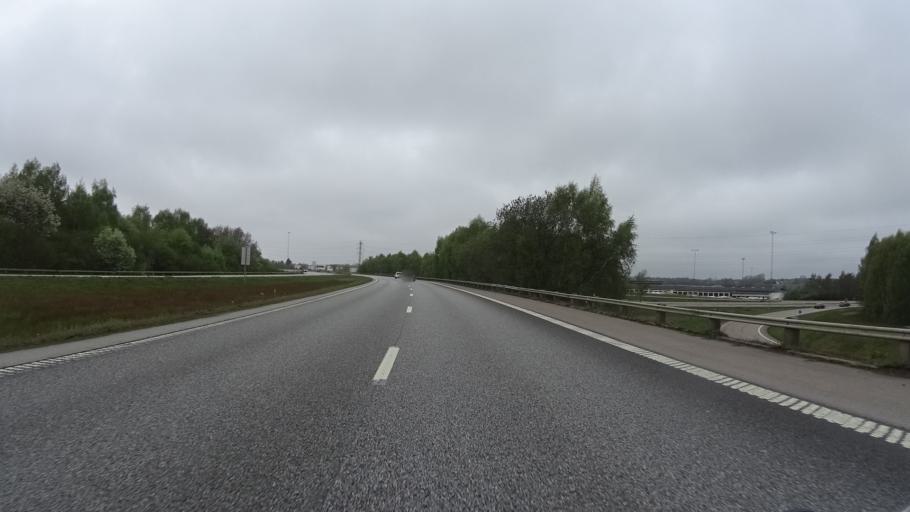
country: SE
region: Skane
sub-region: Helsingborg
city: Gantofta
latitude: 56.0169
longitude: 12.7802
